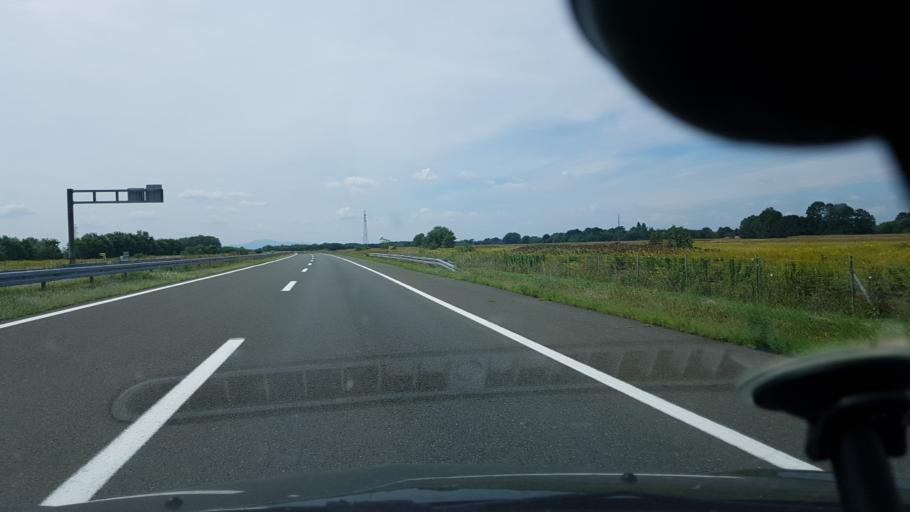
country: HR
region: Medimurska
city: Domasinec
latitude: 46.4067
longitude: 16.5857
